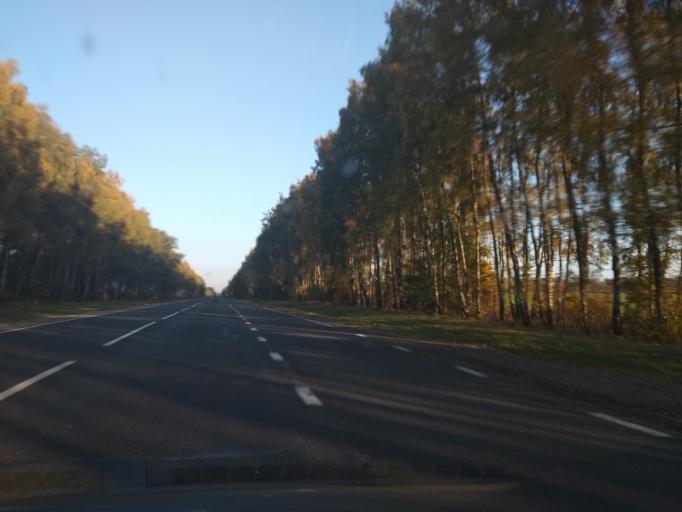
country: BY
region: Grodnenskaya
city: Vawkavysk
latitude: 53.1496
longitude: 24.5671
